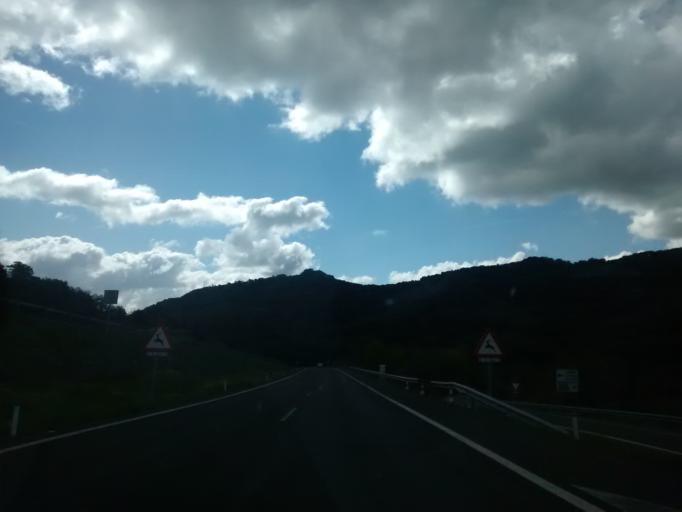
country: ES
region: Basque Country
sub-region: Provincia de Alava
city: Murguia
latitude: 42.9433
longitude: -2.7770
